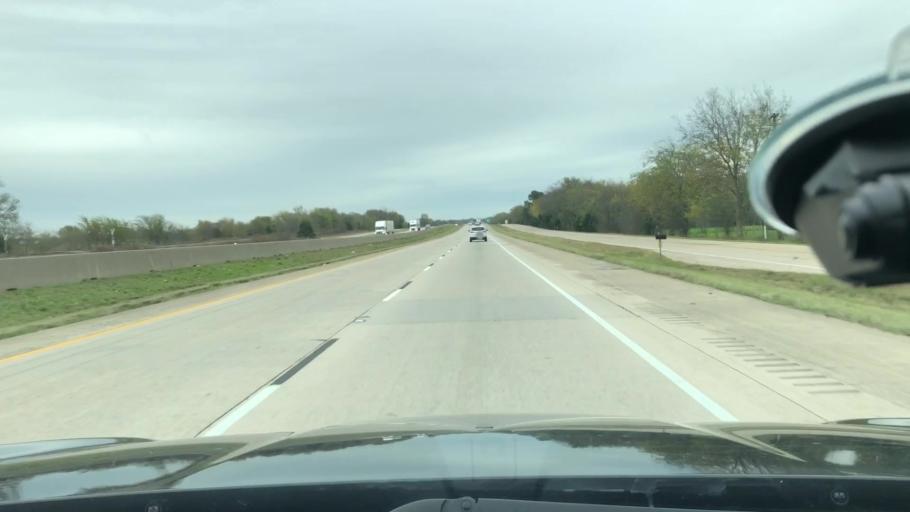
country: US
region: Texas
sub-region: Hunt County
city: Commerce
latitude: 33.1300
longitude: -95.7745
